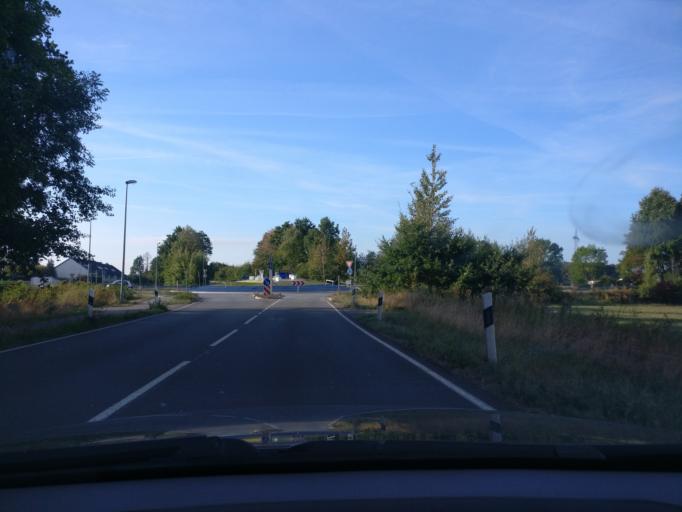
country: DE
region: Lower Saxony
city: Melle
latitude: 52.2000
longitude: 8.3158
